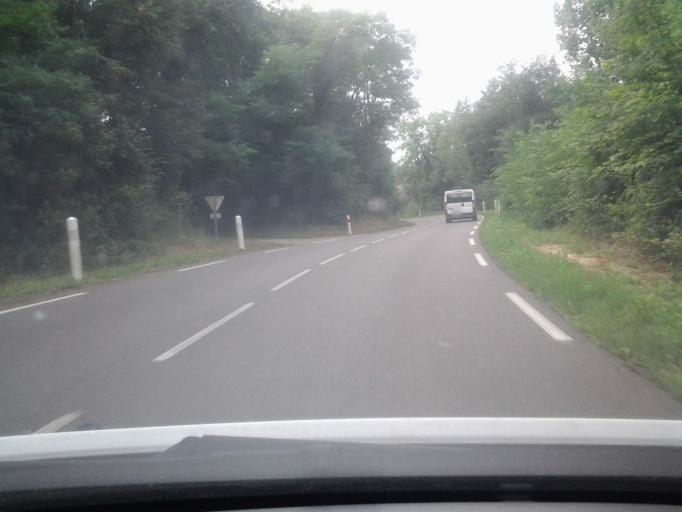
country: FR
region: Pays de la Loire
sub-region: Departement de la Vendee
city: Longeville-sur-Mer
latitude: 46.3916
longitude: -1.4741
